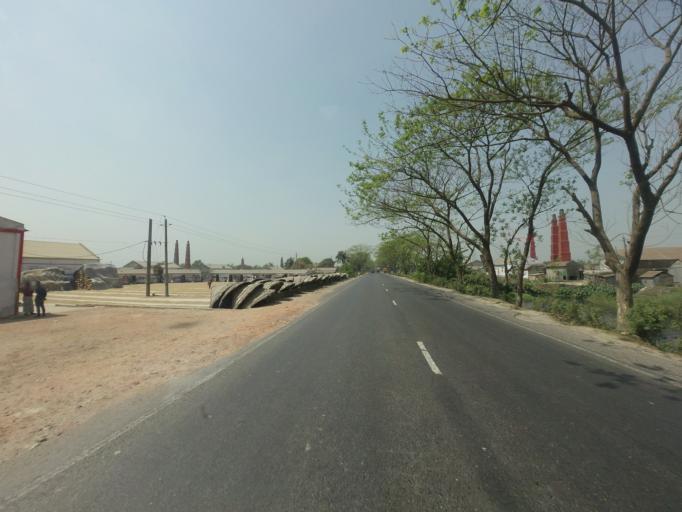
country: BD
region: Dhaka
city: Bhairab Bazar
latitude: 24.0433
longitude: 91.0556
